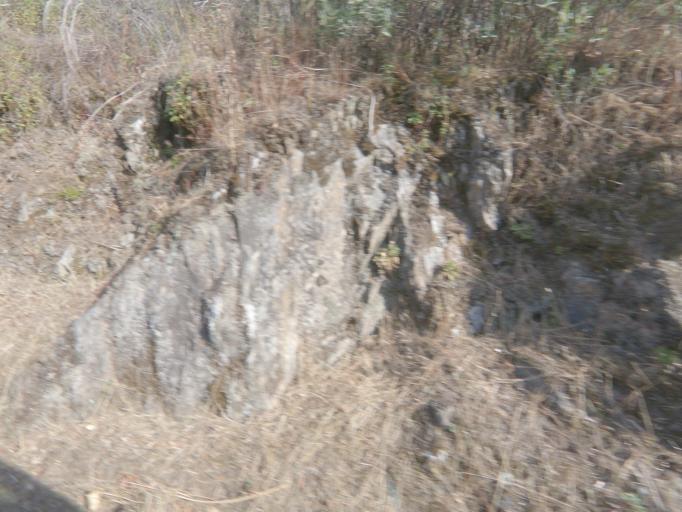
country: PT
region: Vila Real
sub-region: Sabrosa
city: Vilela
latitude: 41.1996
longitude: -7.5425
